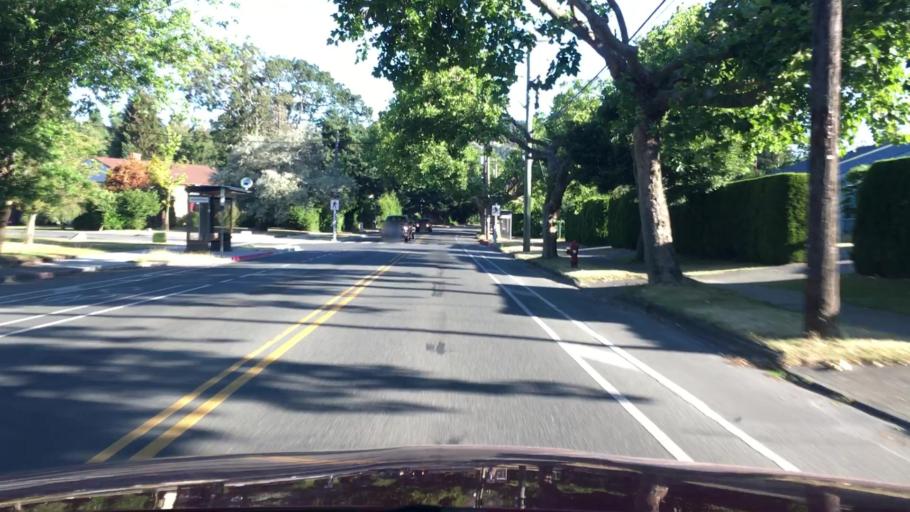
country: CA
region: British Columbia
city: Oak Bay
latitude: 48.4795
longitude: -123.3352
